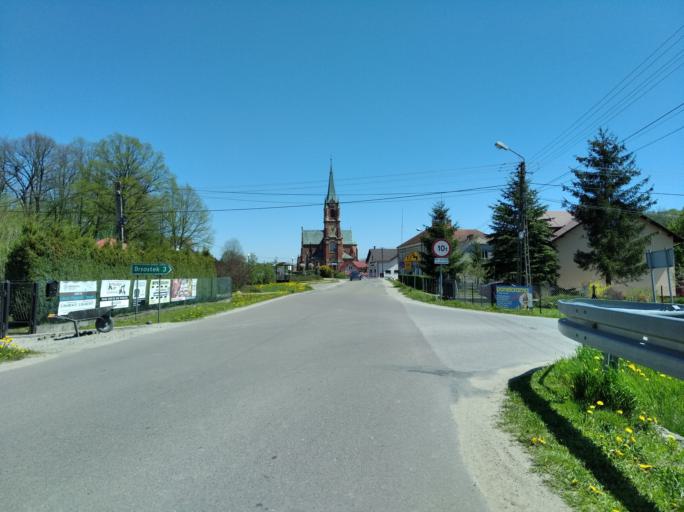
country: PL
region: Subcarpathian Voivodeship
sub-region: Powiat debicki
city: Brzostek
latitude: 49.9146
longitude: 21.4148
